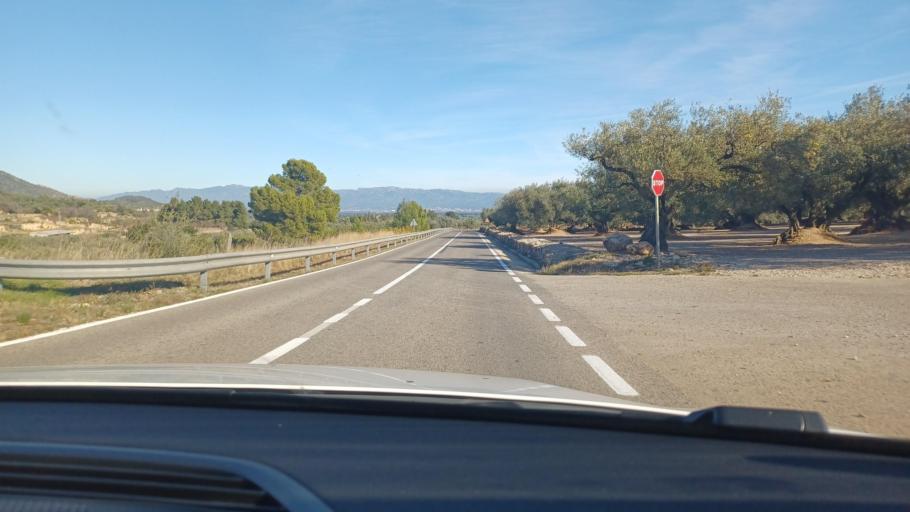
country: ES
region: Catalonia
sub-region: Provincia de Tarragona
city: Mas de Barberans
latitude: 40.7293
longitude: 0.3732
